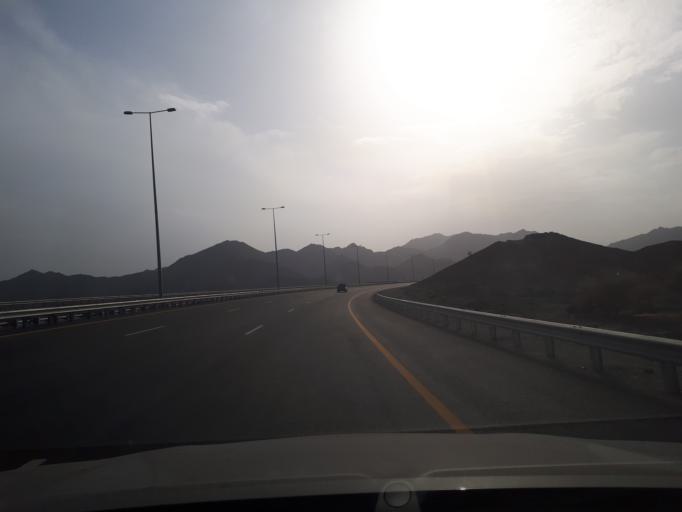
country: OM
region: Ash Sharqiyah
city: Ibra'
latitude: 22.8464
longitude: 58.3371
